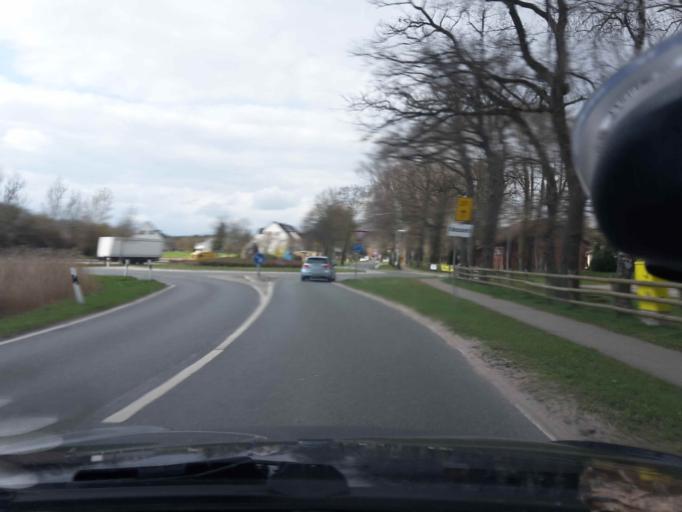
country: DE
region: Lower Saxony
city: Jesteburg
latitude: 53.3008
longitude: 9.9587
